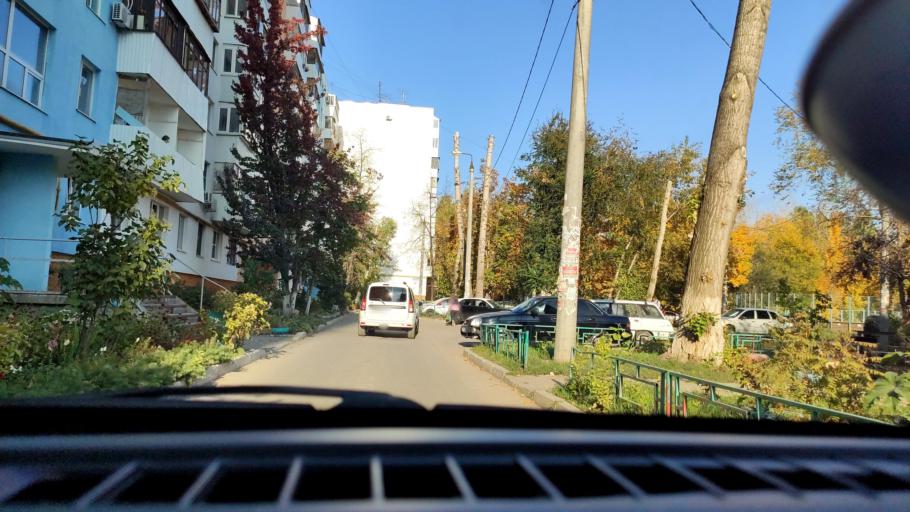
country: RU
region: Samara
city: Samara
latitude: 53.2573
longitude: 50.2368
